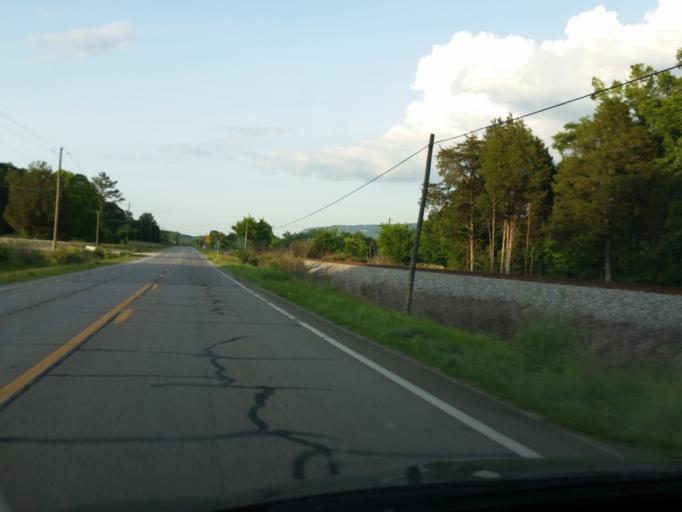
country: US
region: Georgia
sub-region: Walker County
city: Chattanooga Valley
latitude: 34.9462
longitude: -85.4436
